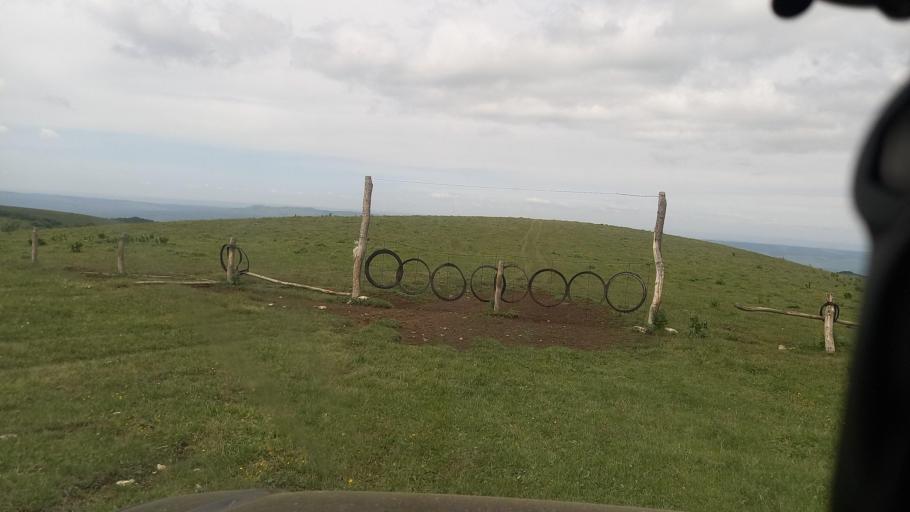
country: RU
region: Karachayevo-Cherkesiya
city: Pregradnaya
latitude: 43.9921
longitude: 41.2859
